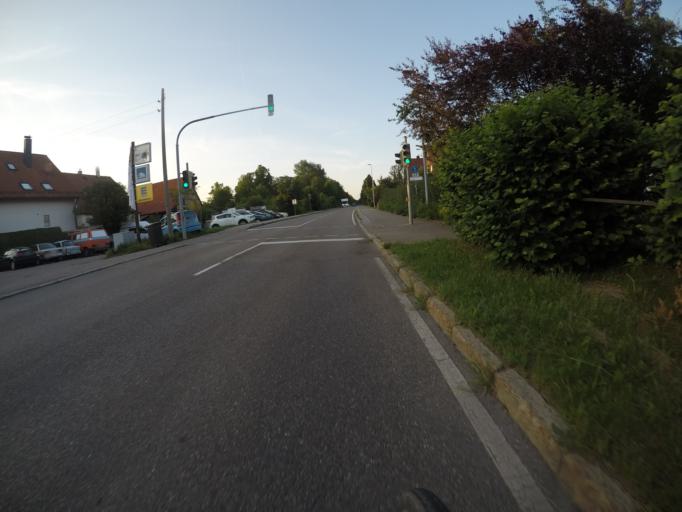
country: DE
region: Baden-Wuerttemberg
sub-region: Regierungsbezirk Stuttgart
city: Steinenbronn
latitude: 48.6667
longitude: 9.1241
